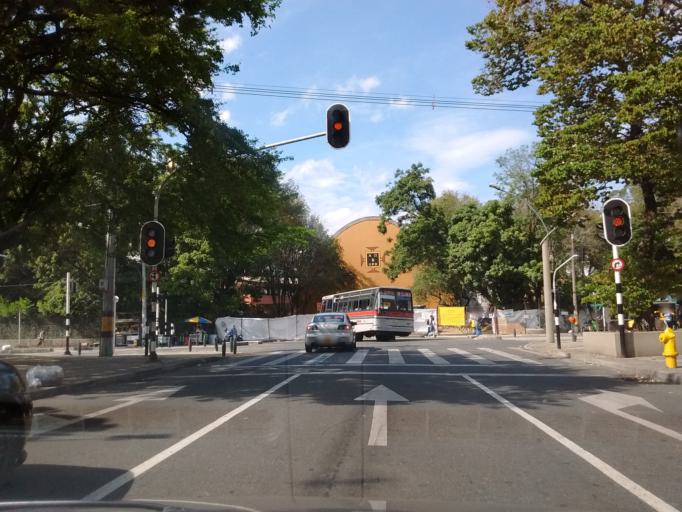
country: CO
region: Antioquia
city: Medellin
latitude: 6.2448
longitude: -75.5894
